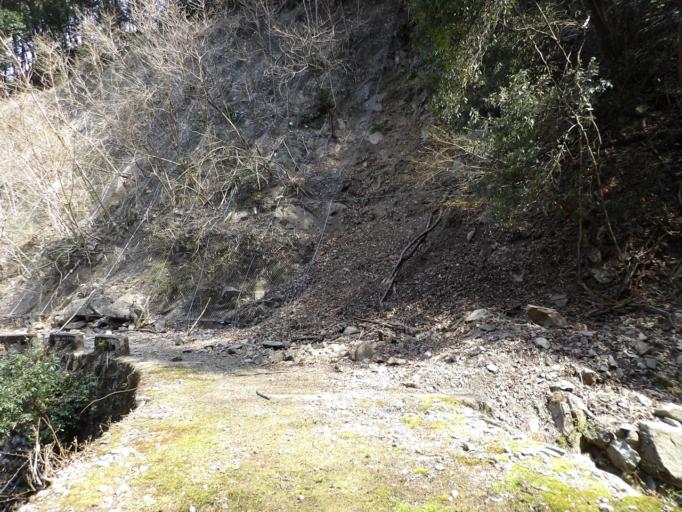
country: JP
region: Shizuoka
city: Mori
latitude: 35.1396
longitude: 137.8184
